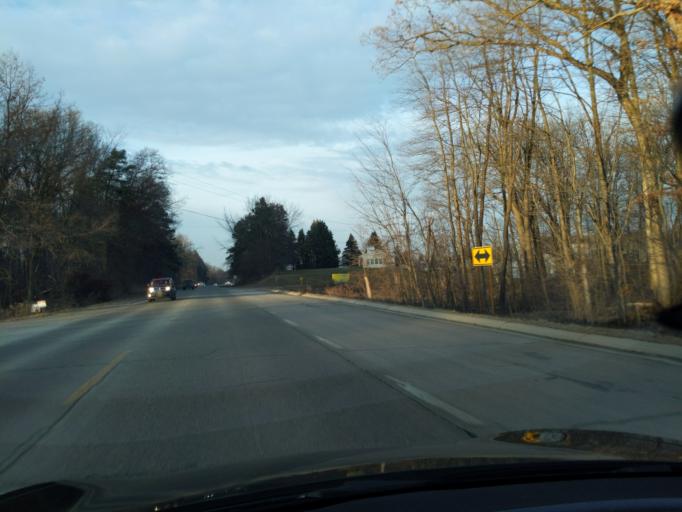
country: US
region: Michigan
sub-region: Livingston County
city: Brighton
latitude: 42.5890
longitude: -83.7539
